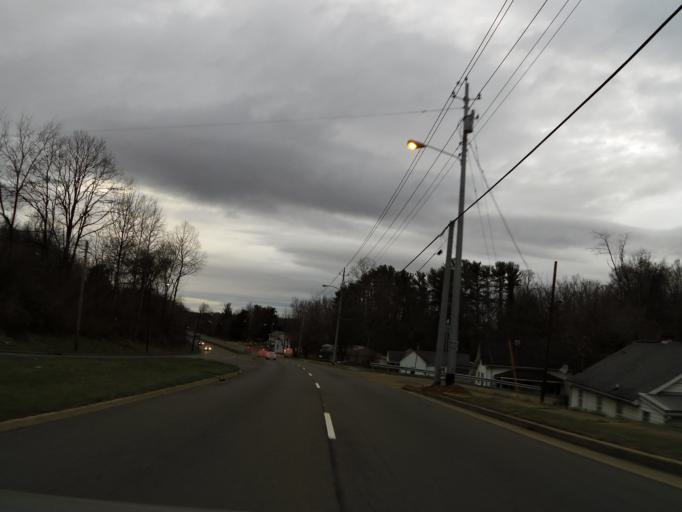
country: US
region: Tennessee
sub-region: Washington County
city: Johnson City
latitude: 36.3024
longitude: -82.3558
